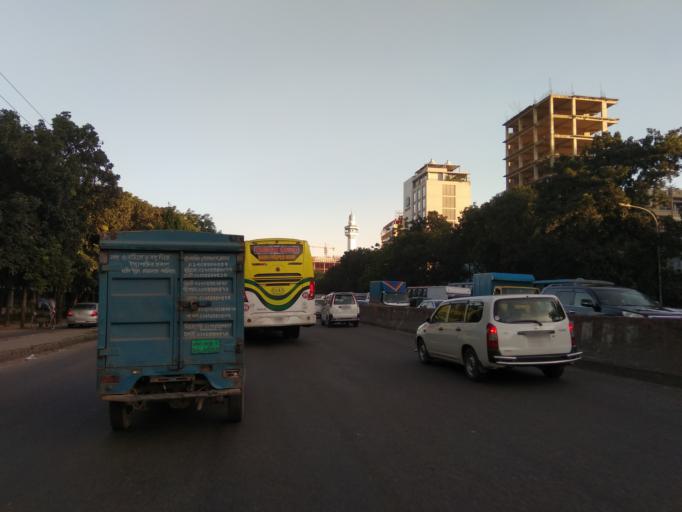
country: BD
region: Dhaka
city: Tungi
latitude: 23.8563
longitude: 90.4036
